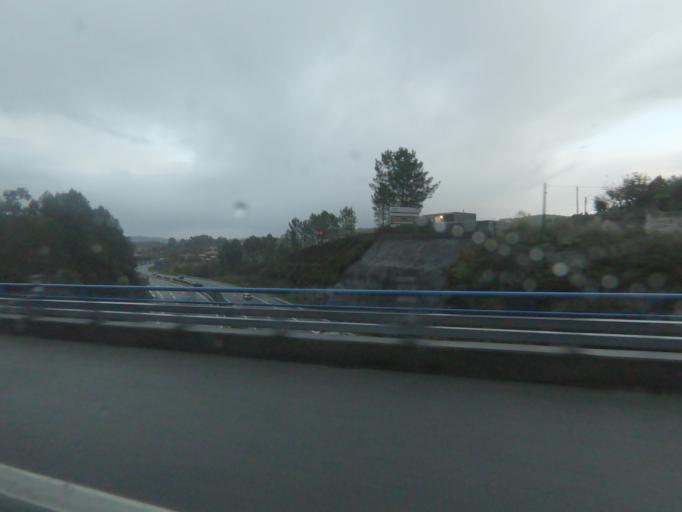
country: PT
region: Braga
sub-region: Braga
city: Oliveira
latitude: 41.5314
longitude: -8.4851
